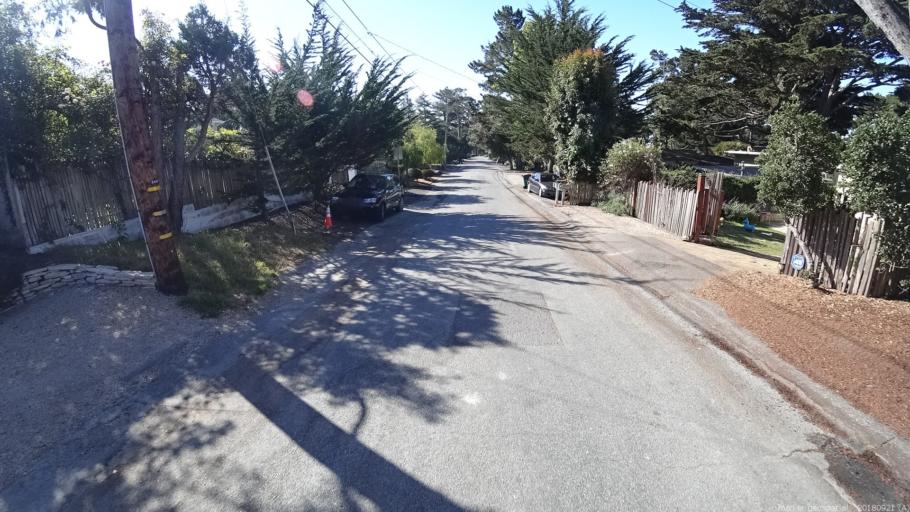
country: US
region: California
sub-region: Monterey County
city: Carmel-by-the-Sea
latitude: 36.5626
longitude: -121.9174
